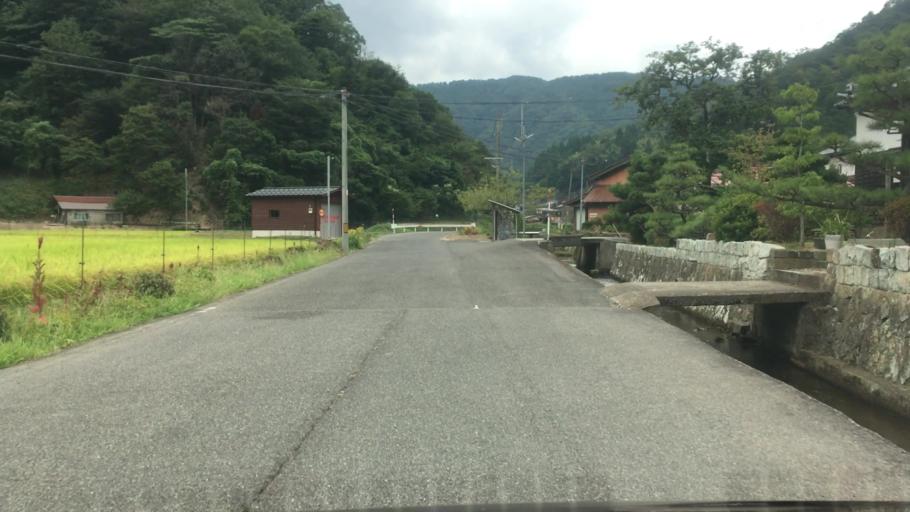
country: JP
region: Hyogo
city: Toyooka
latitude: 35.6337
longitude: 134.6793
